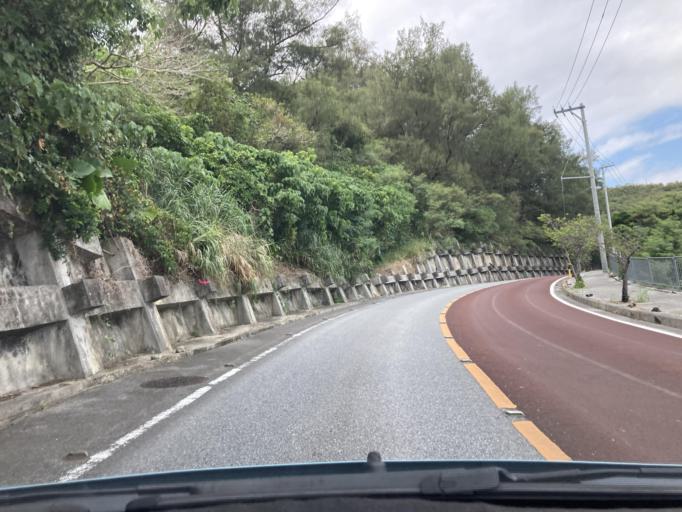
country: JP
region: Okinawa
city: Ginowan
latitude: 26.2612
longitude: 127.7839
